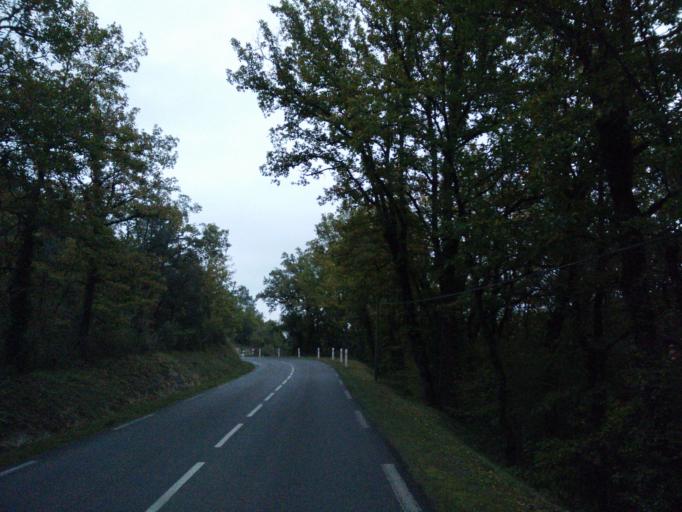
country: FR
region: Midi-Pyrenees
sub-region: Departement du Lot
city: Gourdon
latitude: 44.7806
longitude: 1.3228
